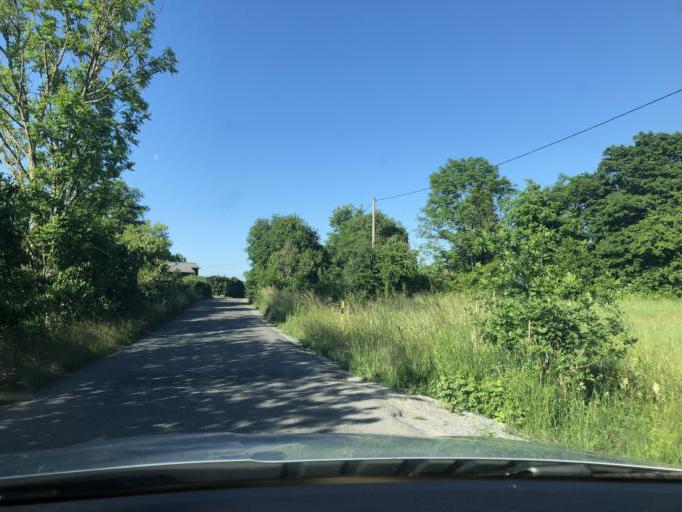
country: SE
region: Blekinge
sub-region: Karlshamns Kommun
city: Karlshamn
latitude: 56.1690
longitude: 14.8144
